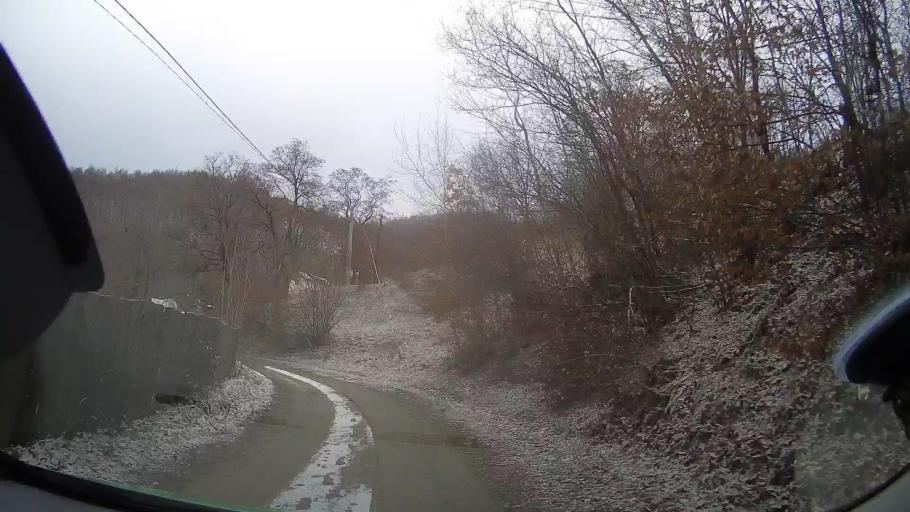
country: RO
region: Cluj
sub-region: Comuna Valea Ierii
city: Valea Ierii
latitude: 46.6525
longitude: 23.3466
